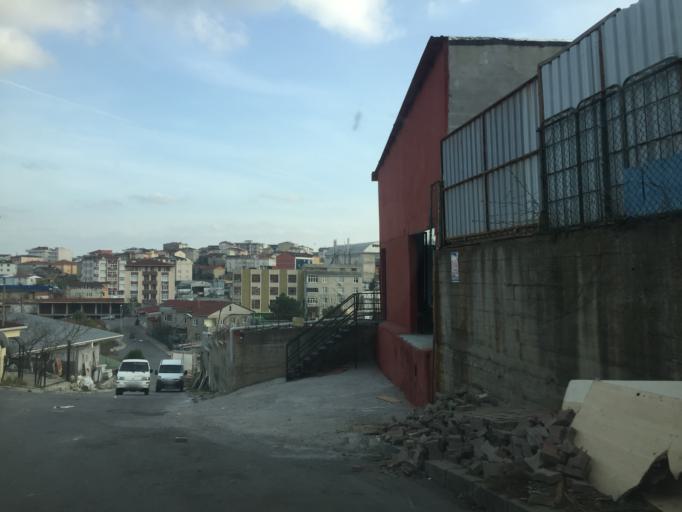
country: TR
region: Istanbul
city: Sultanbeyli
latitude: 40.9475
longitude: 29.2961
